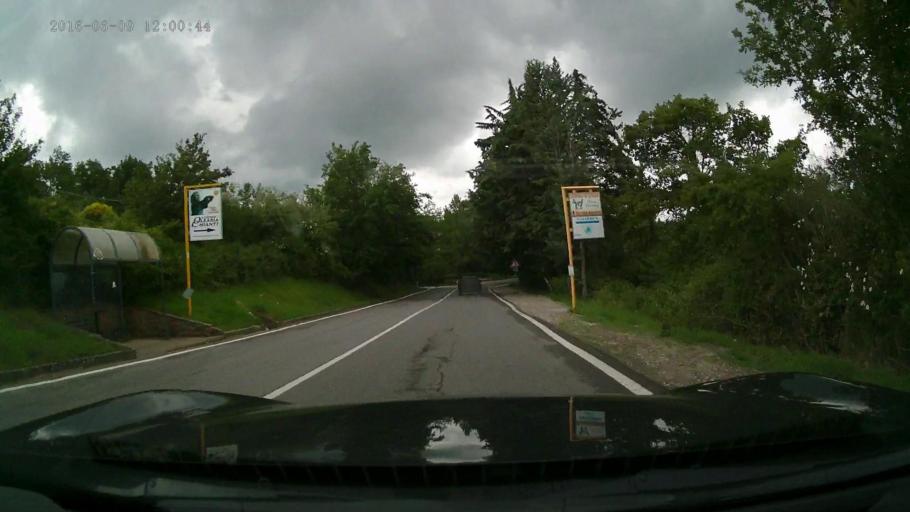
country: IT
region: Tuscany
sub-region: Province of Florence
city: Panzano in Chianti
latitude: 43.5384
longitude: 11.3168
